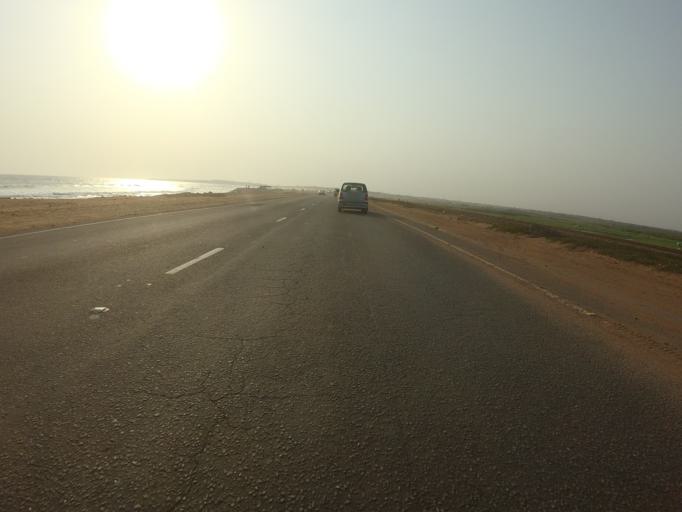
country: GH
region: Greater Accra
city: Nungua
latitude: 5.6137
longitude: -0.0304
